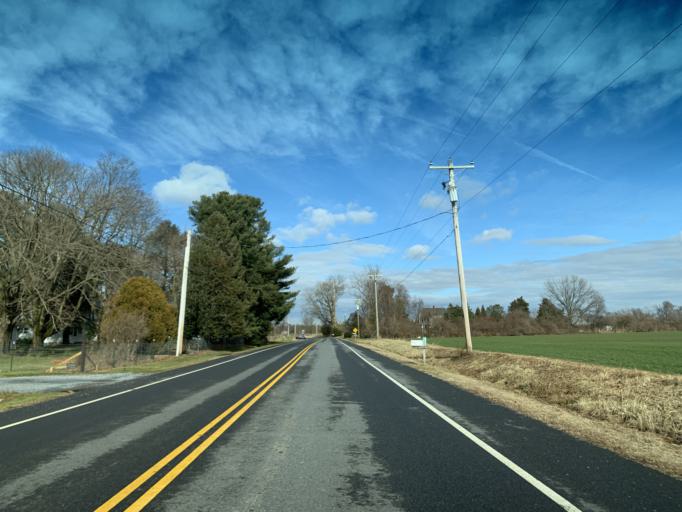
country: US
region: Maryland
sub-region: Kent County
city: Chestertown
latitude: 39.3464
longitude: -76.0621
